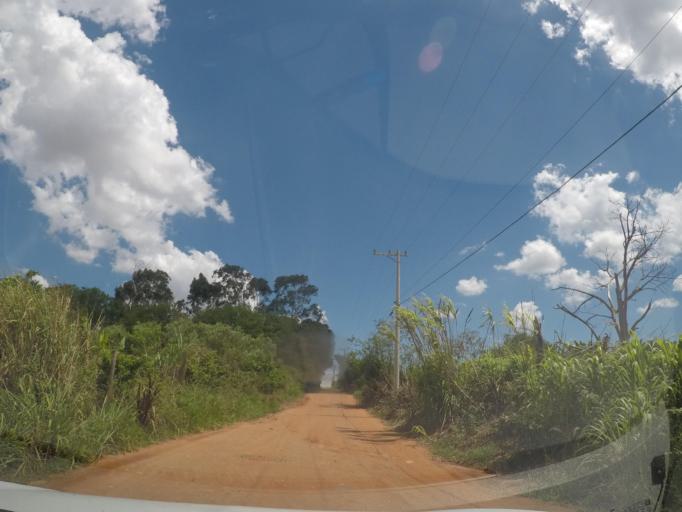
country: BR
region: Sao Paulo
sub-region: Sumare
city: Sumare
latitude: -22.8417
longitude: -47.2476
